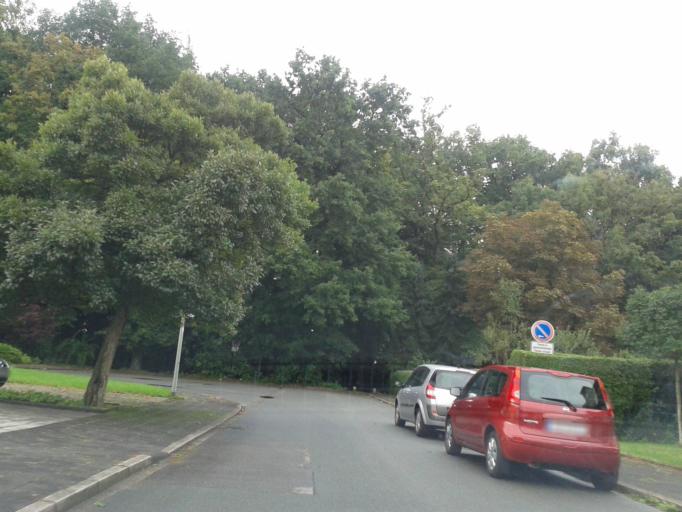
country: DE
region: North Rhine-Westphalia
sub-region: Regierungsbezirk Detmold
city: Paderborn
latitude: 51.7427
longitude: 8.7471
